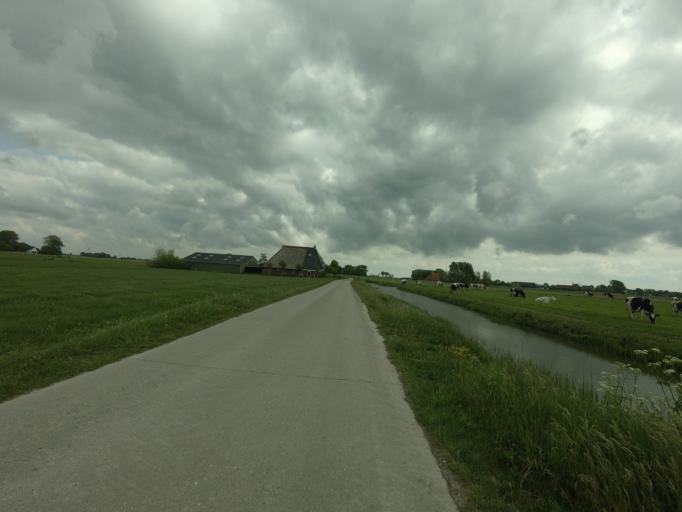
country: NL
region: Friesland
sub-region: Gemeente Littenseradiel
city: Wommels
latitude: 53.1080
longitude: 5.6173
